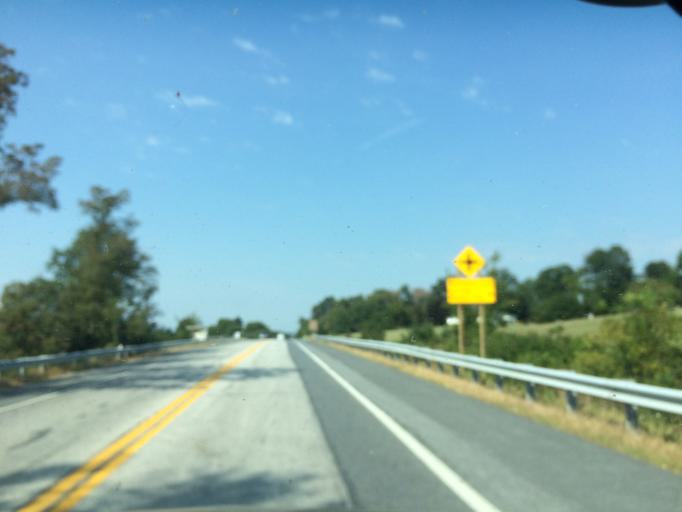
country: US
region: Maryland
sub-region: Carroll County
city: New Windsor
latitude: 39.5452
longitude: -77.0900
